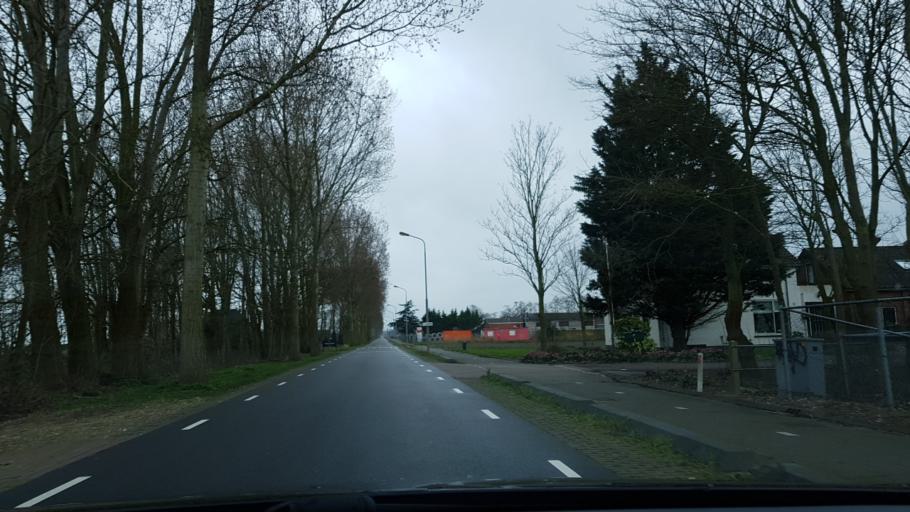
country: NL
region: North Holland
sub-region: Gemeente Haarlemmermeer
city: Hoofddorp
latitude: 52.2674
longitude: 4.6779
